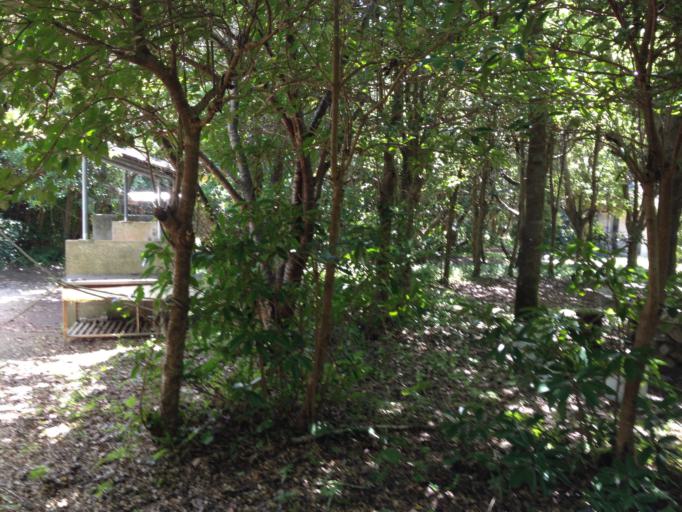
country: JP
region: Wakayama
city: Shingu
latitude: 33.4451
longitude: 135.7820
